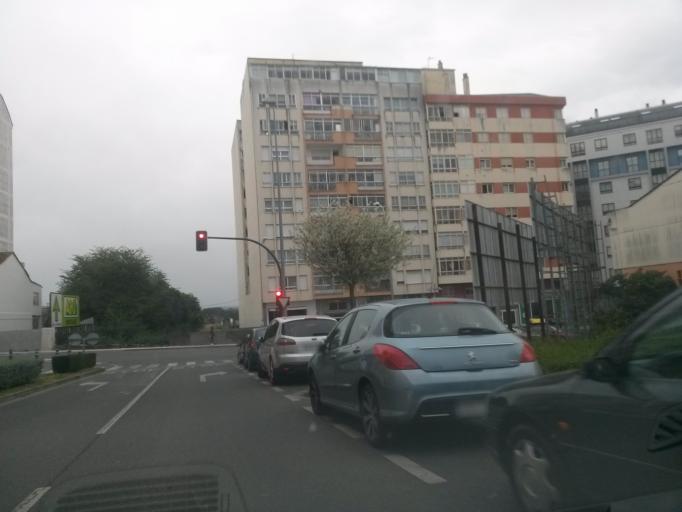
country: ES
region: Galicia
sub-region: Provincia de Lugo
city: Lugo
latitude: 43.0271
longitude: -7.5692
